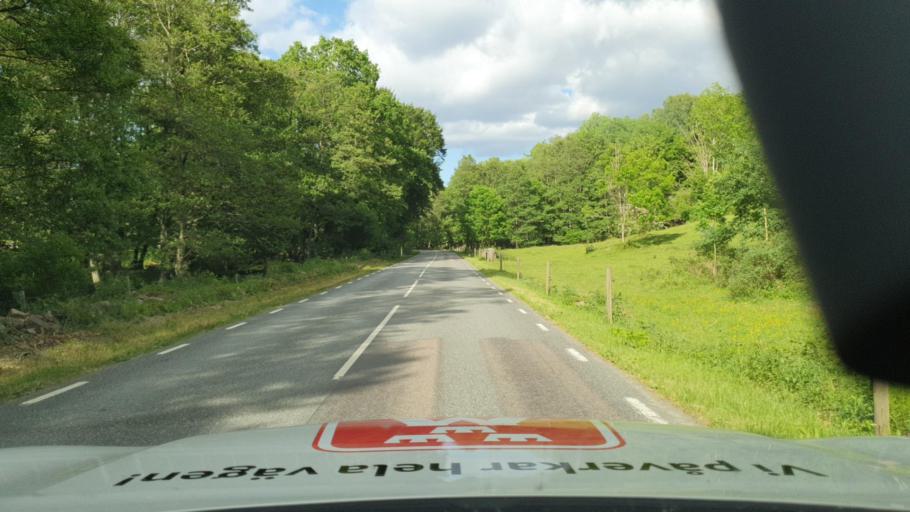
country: SE
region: Skane
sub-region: Simrishamns Kommun
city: Kivik
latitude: 55.6194
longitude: 14.2421
